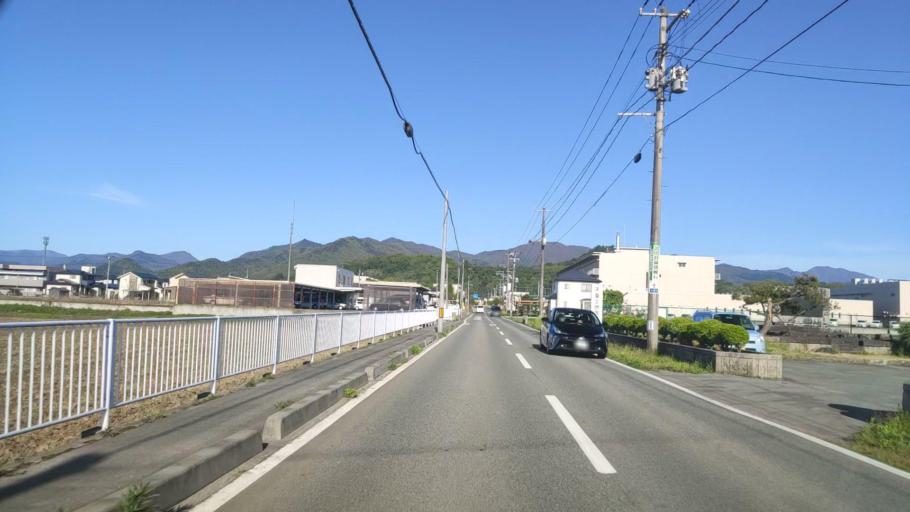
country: JP
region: Yamagata
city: Tendo
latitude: 38.3555
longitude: 140.3605
